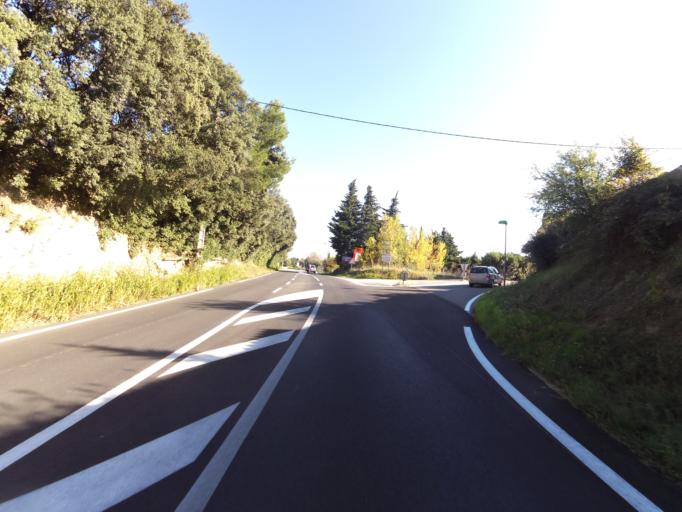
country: FR
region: Provence-Alpes-Cote d'Azur
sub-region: Departement du Vaucluse
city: Loriol-du-Comtat
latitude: 44.0705
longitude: 5.0108
